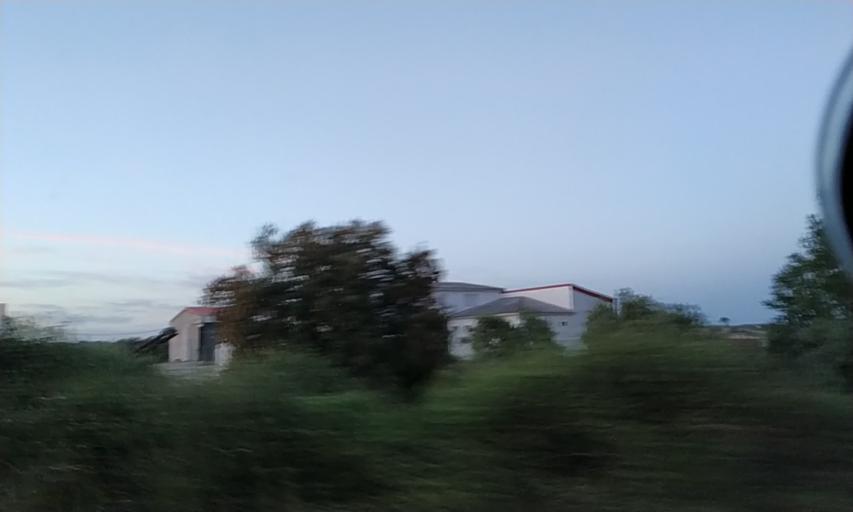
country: ES
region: Extremadura
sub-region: Provincia de Caceres
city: Piedras Albas
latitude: 39.7632
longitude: -6.9083
